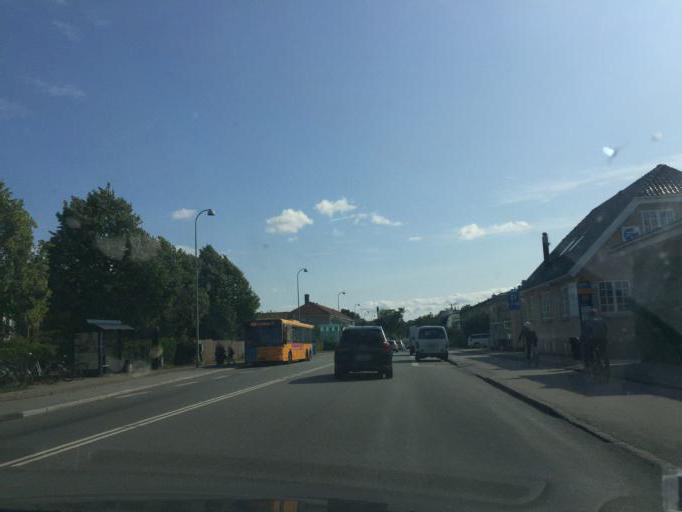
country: DK
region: Capital Region
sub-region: Herlev Kommune
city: Herlev
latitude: 55.7225
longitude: 12.4716
